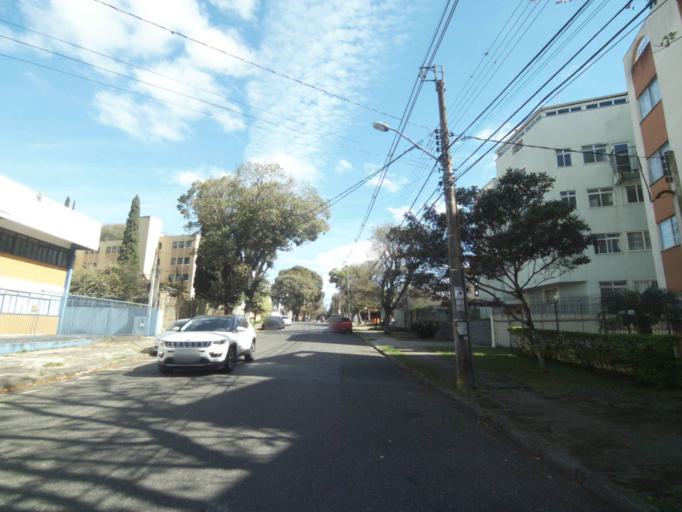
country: BR
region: Parana
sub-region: Curitiba
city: Curitiba
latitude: -25.4618
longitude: -49.2792
